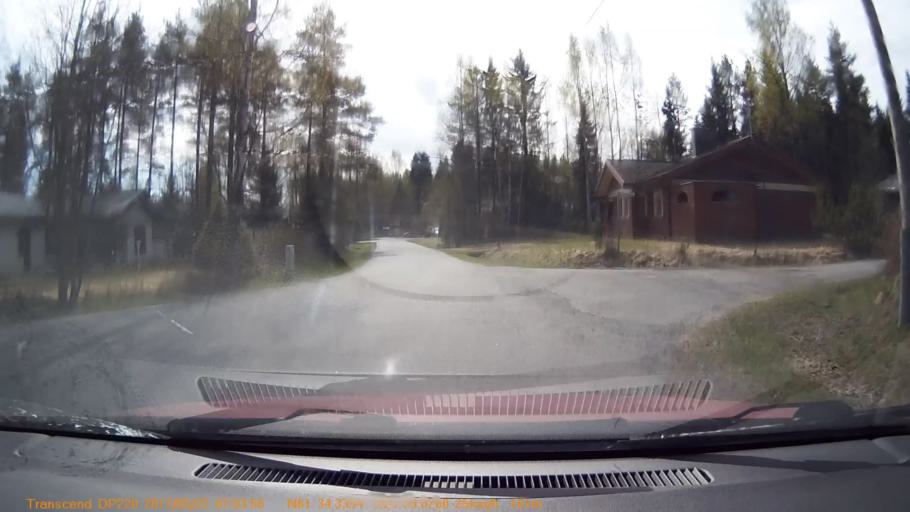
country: FI
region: Pirkanmaa
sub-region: Tampere
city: Yloejaervi
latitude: 61.5723
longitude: 23.4969
